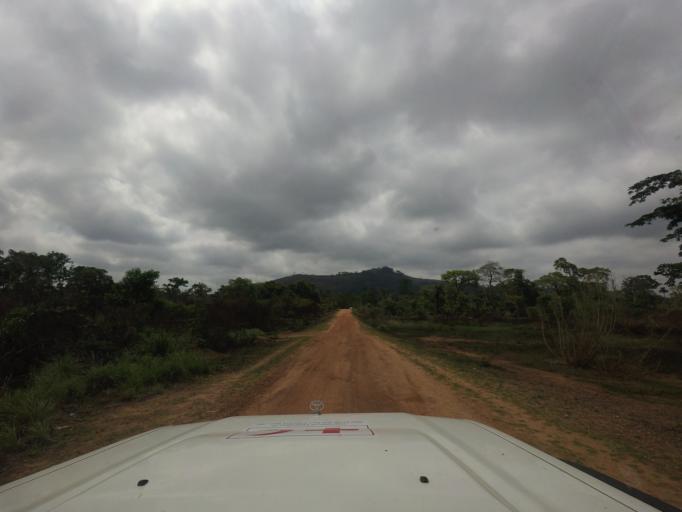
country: LR
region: Lofa
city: Voinjama
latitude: 8.4149
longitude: -9.7363
